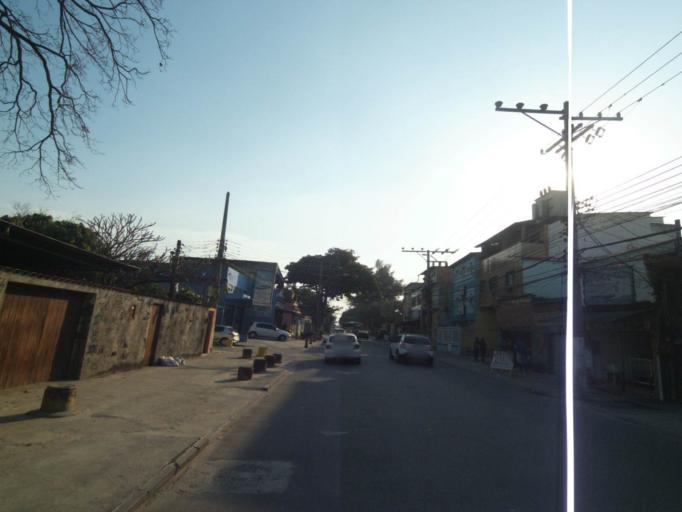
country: BR
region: Rio de Janeiro
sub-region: Nilopolis
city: Nilopolis
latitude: -22.8766
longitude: -43.4258
